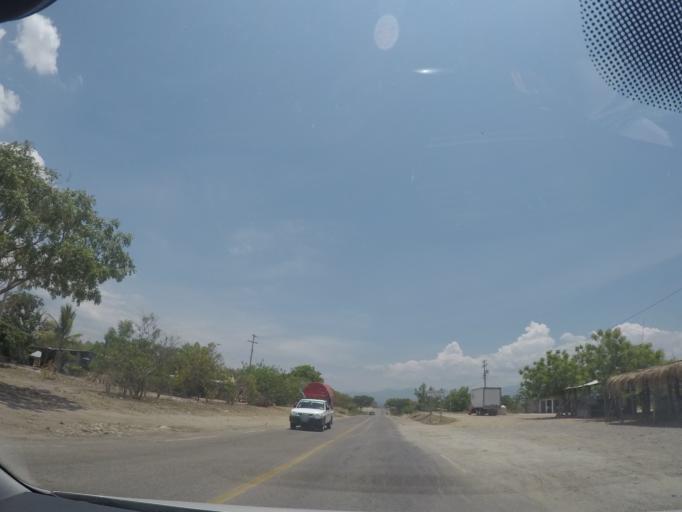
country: MX
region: Oaxaca
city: Santa Maria Jalapa del Marques
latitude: 16.4393
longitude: -95.5067
